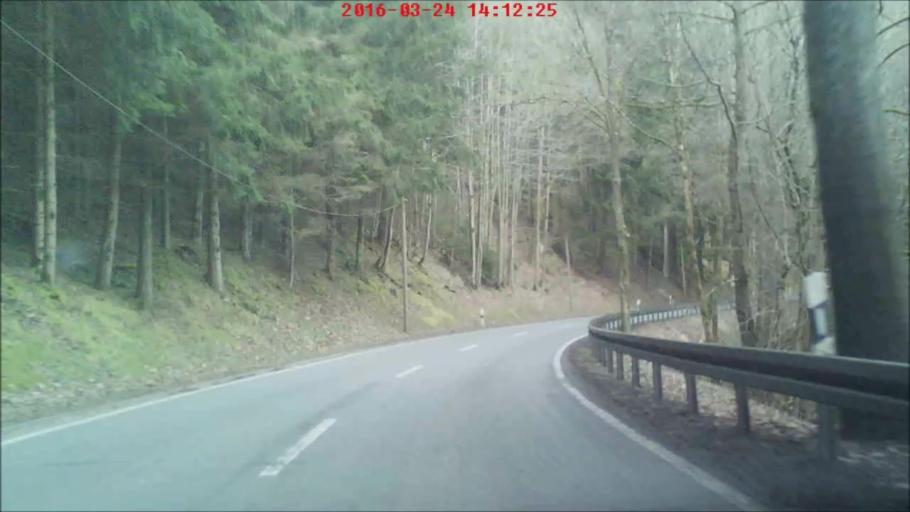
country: DE
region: Thuringia
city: Wildenspring
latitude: 50.5853
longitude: 11.0762
